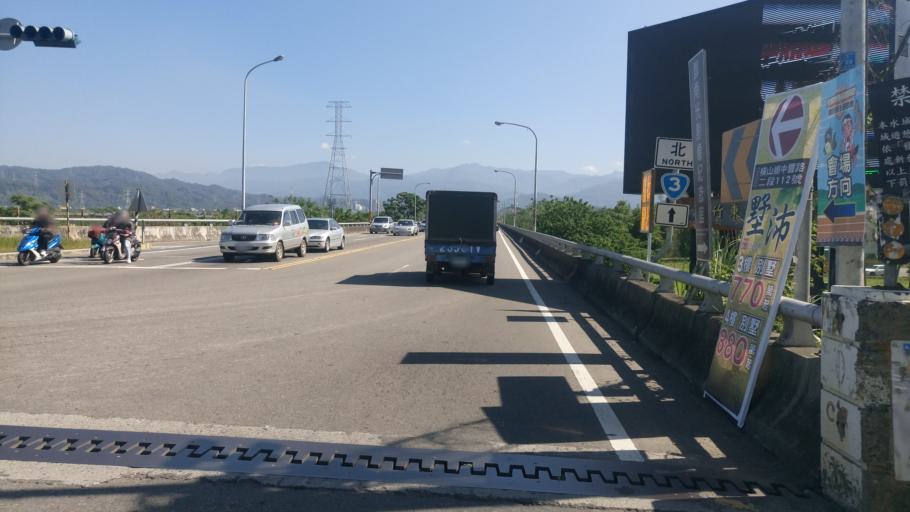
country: TW
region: Taiwan
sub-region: Hsinchu
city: Zhubei
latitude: 24.7230
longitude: 121.1018
